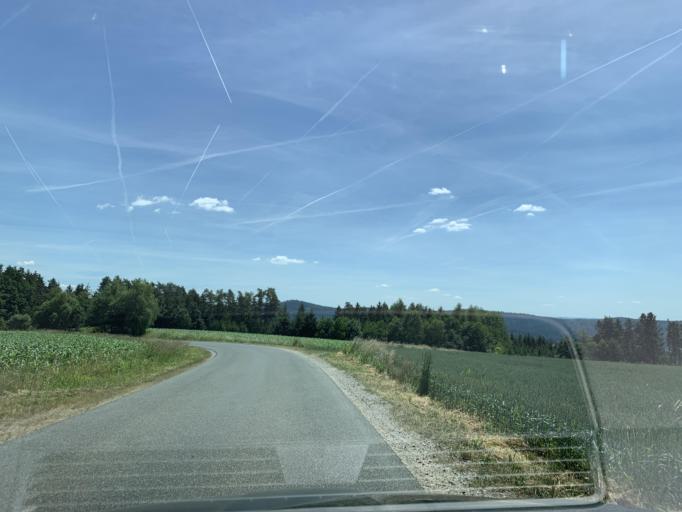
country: DE
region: Bavaria
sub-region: Upper Palatinate
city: Dieterskirchen
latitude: 49.4205
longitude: 12.4016
